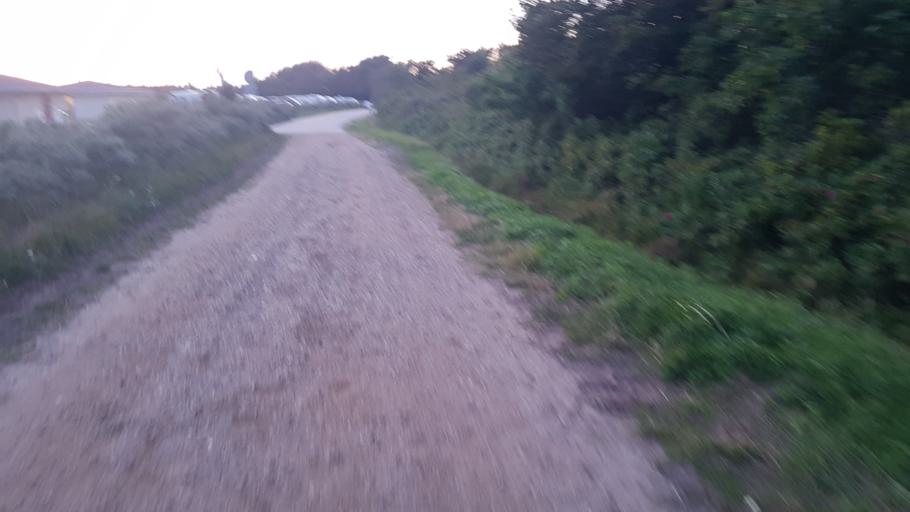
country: DE
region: Schleswig-Holstein
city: List
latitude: 55.0912
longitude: 8.5407
